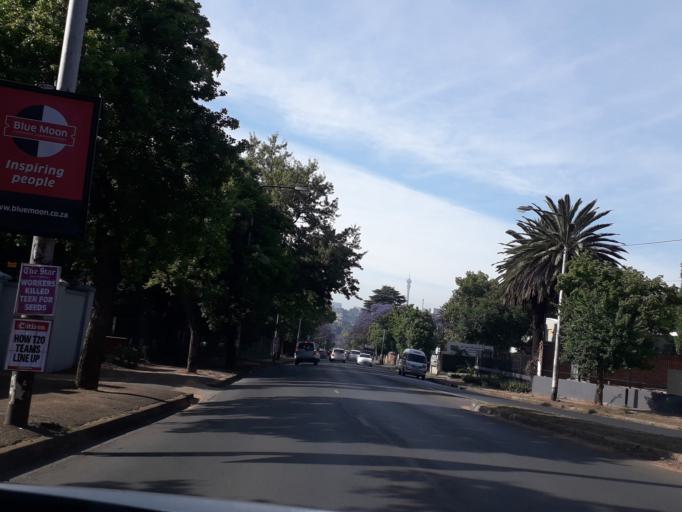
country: ZA
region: Gauteng
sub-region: City of Johannesburg Metropolitan Municipality
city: Johannesburg
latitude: -26.1534
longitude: 28.0457
